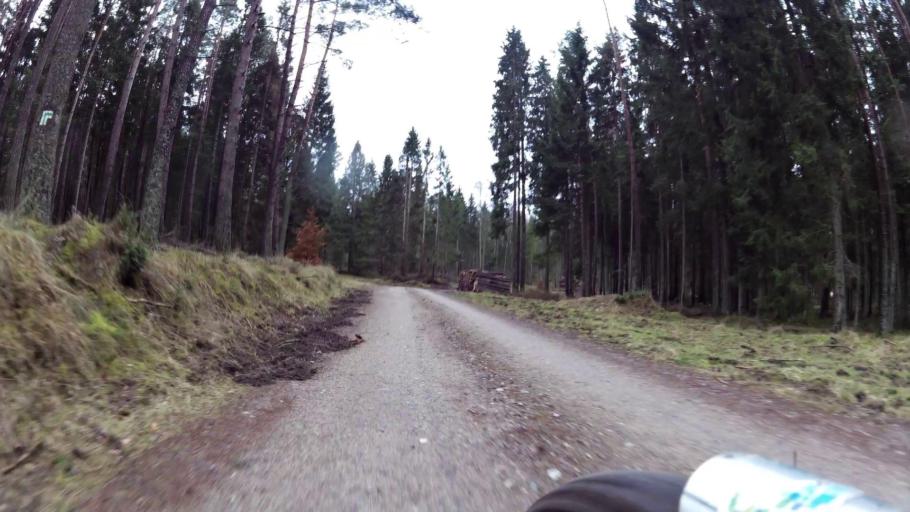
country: PL
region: Pomeranian Voivodeship
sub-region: Powiat bytowski
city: Borzytuchom
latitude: 54.2548
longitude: 17.3118
